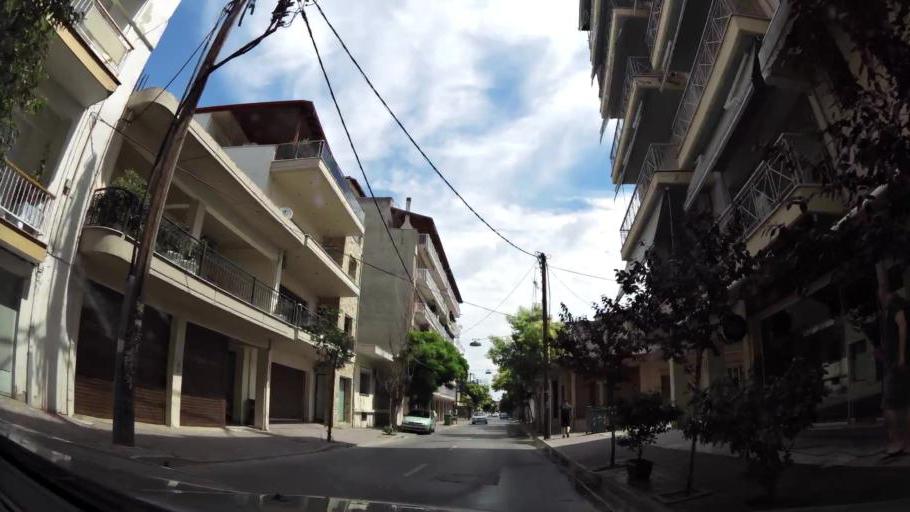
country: GR
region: Central Macedonia
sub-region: Nomos Pierias
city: Katerini
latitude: 40.2750
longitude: 22.5033
